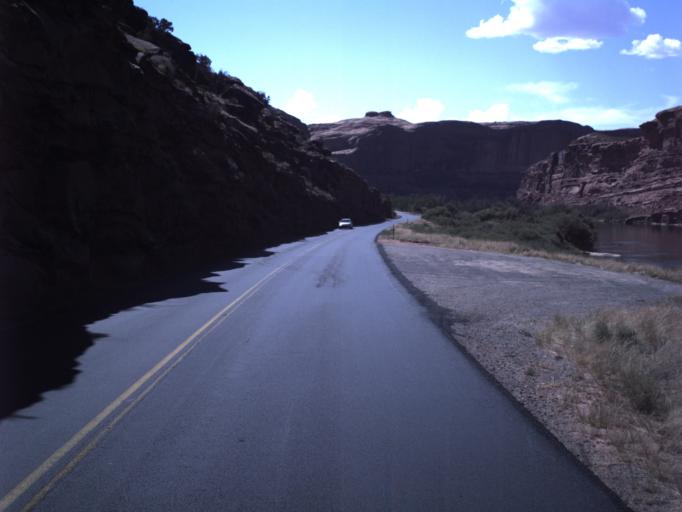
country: US
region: Utah
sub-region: Grand County
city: Moab
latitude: 38.6158
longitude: -109.5272
